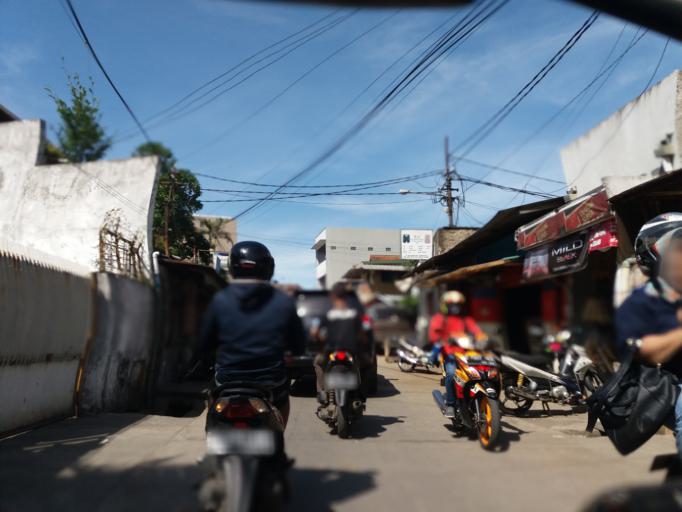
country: ID
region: West Java
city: Bandung
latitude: -6.9352
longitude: 107.5988
